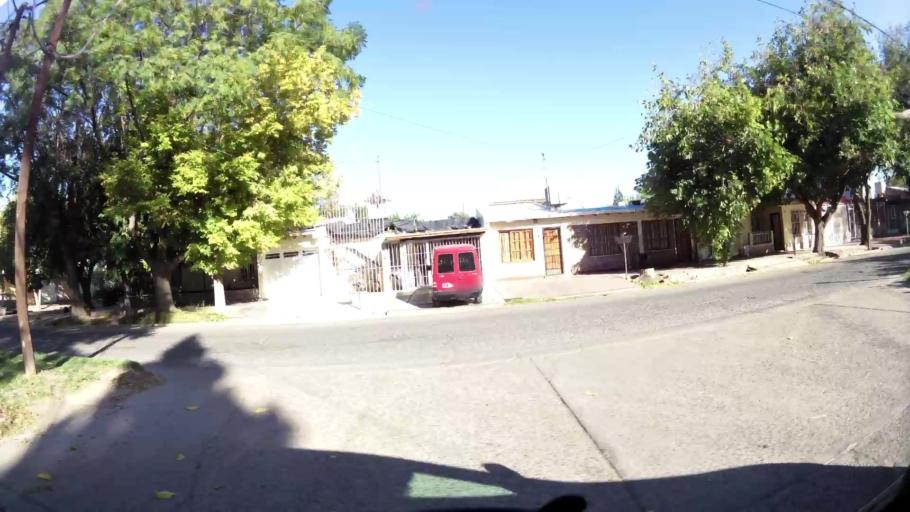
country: AR
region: Mendoza
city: Las Heras
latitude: -32.8553
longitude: -68.8147
